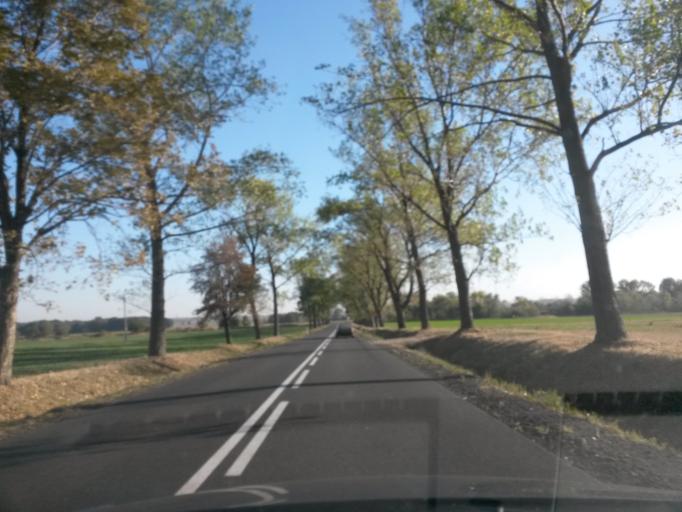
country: PL
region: Lower Silesian Voivodeship
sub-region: Powiat sredzki
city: Udanin
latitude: 51.0275
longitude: 16.4034
